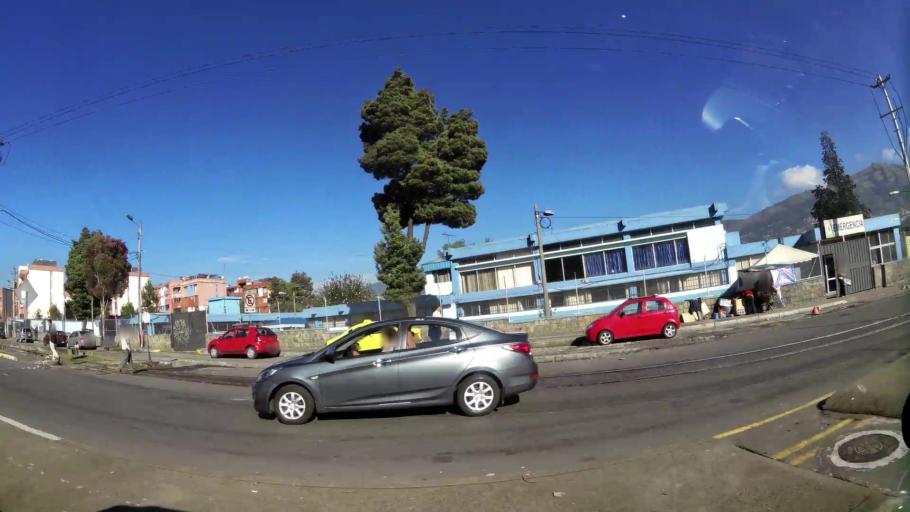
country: EC
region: Pichincha
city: Quito
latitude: -0.2464
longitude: -78.5185
